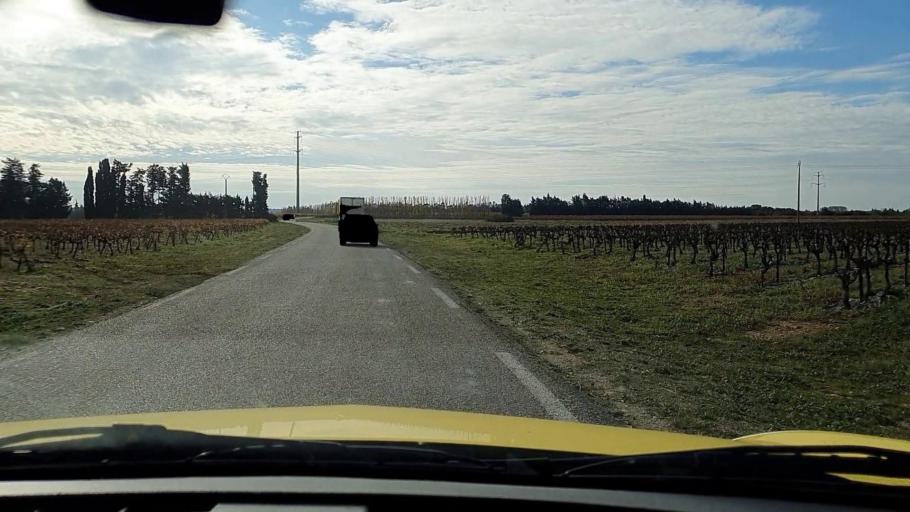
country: FR
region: Languedoc-Roussillon
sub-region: Departement du Gard
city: Jonquieres-Saint-Vincent
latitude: 43.8451
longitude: 4.5724
